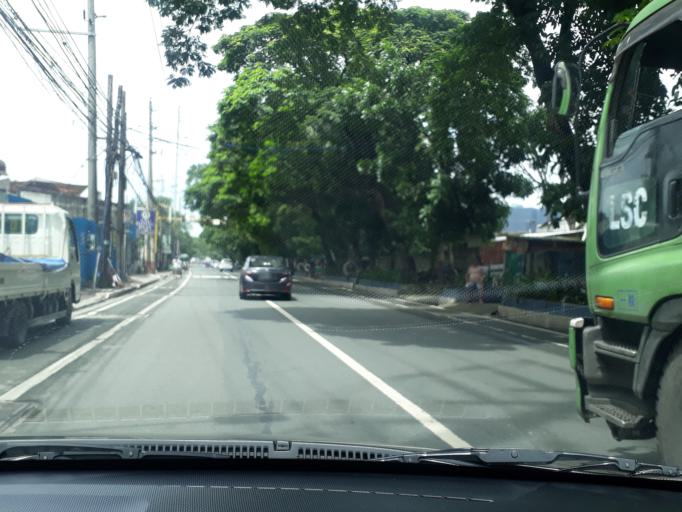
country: PH
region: Metro Manila
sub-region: Marikina
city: Calumpang
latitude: 14.5965
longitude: 121.0893
